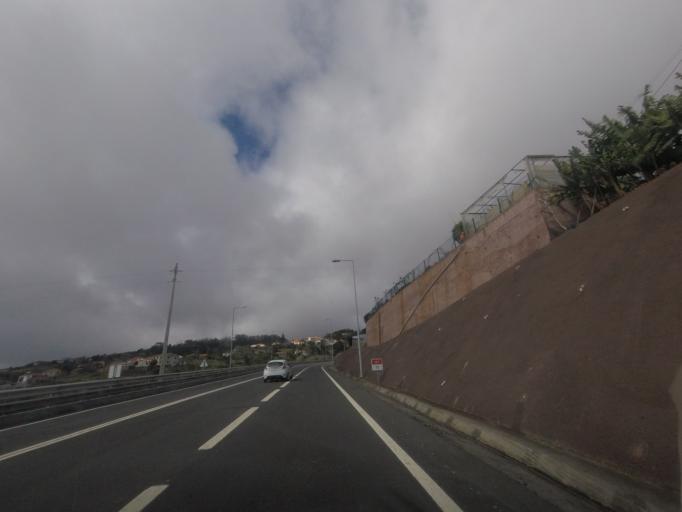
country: PT
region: Madeira
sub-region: Calheta
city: Estreito da Calheta
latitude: 32.7357
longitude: -17.1957
